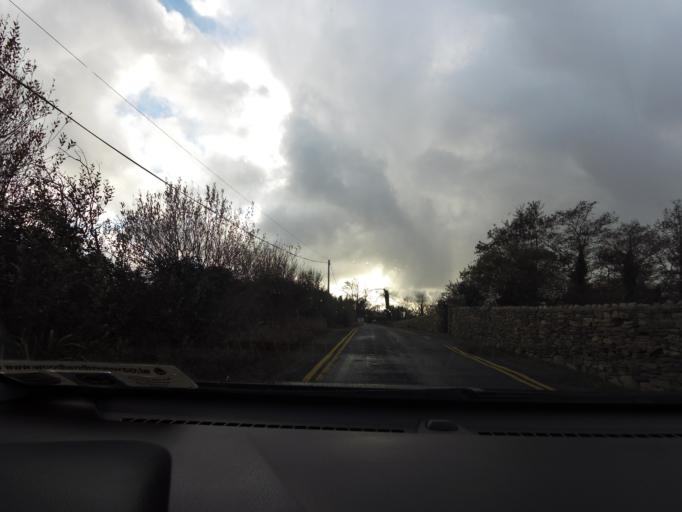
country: IE
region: Connaught
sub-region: Maigh Eo
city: Westport
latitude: 53.7751
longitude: -9.7724
